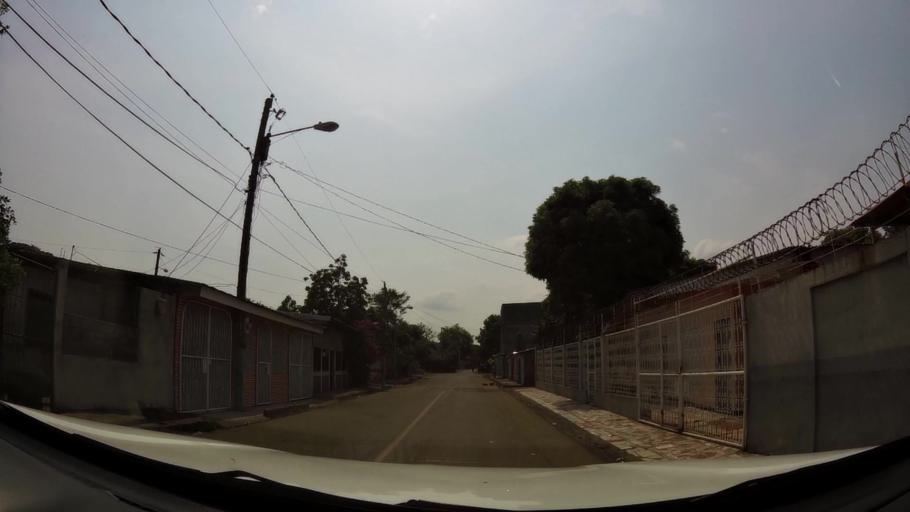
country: NI
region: Managua
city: Ciudad Sandino
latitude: 12.1279
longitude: -86.3145
